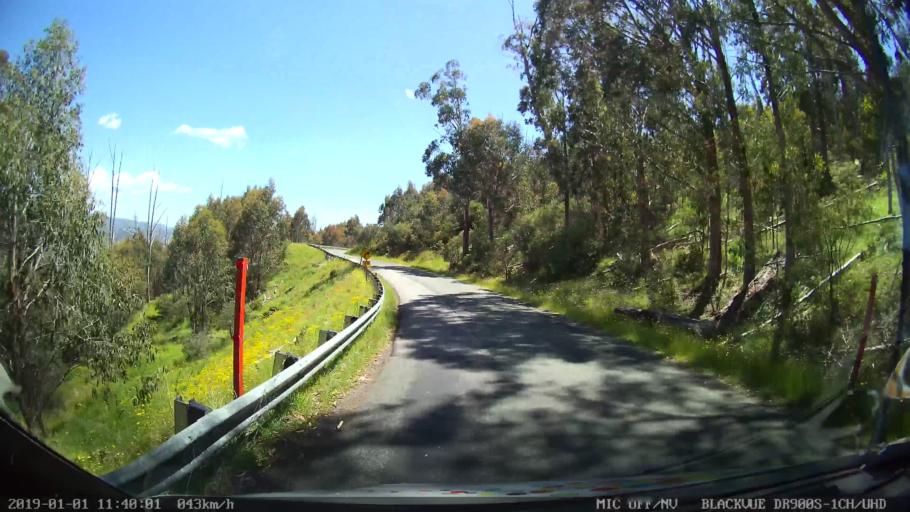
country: AU
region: New South Wales
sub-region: Snowy River
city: Jindabyne
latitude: -35.9229
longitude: 148.3861
